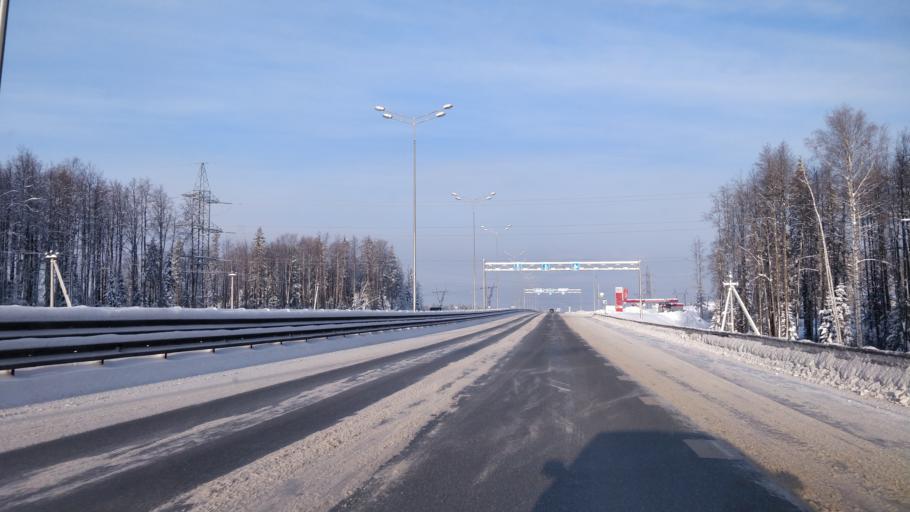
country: RU
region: Perm
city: Novyye Lyady
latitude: 58.0383
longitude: 56.4332
